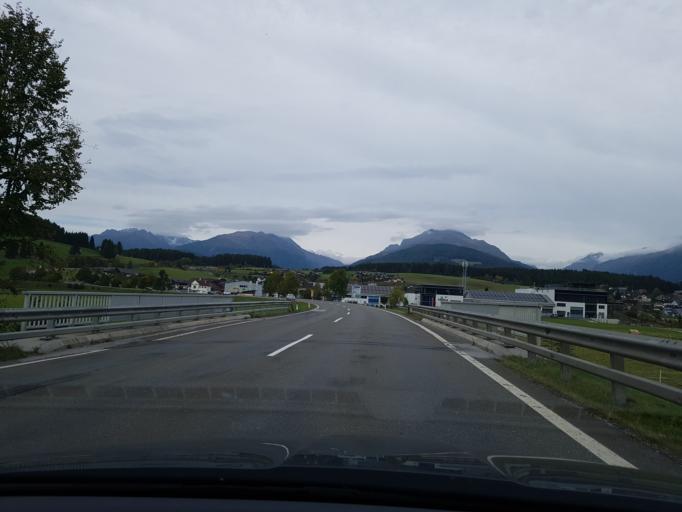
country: AT
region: Salzburg
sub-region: Politischer Bezirk Tamsweg
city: Tamsweg
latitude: 47.1295
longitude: 13.7955
